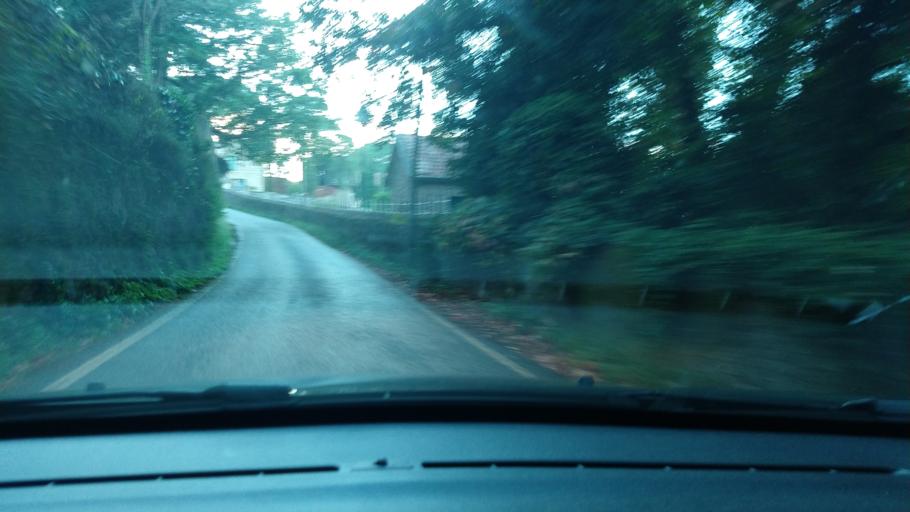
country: PT
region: Lisbon
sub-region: Sintra
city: Sintra
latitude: 38.7907
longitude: -9.4077
